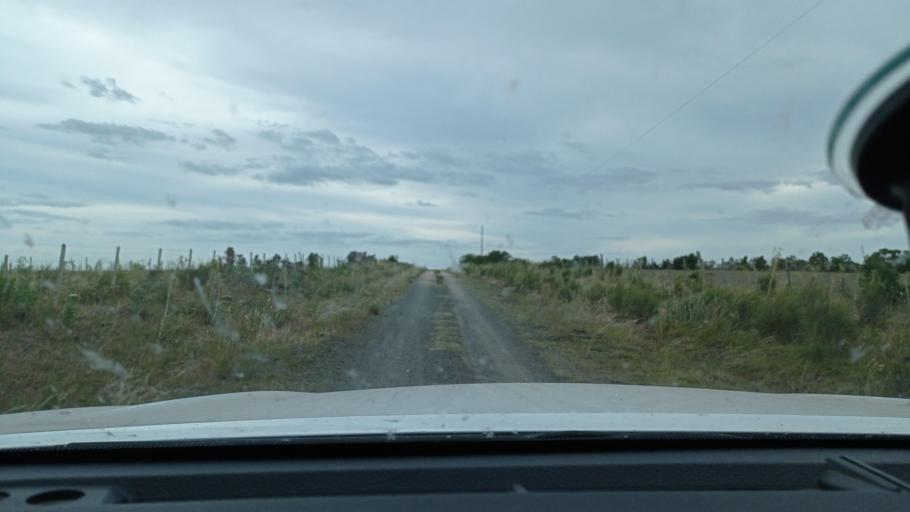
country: UY
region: Florida
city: Casupa
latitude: -34.1459
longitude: -55.7958
